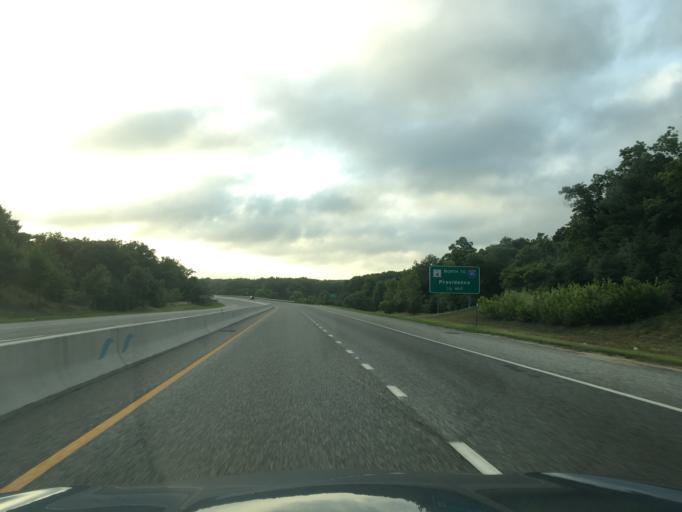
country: US
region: Rhode Island
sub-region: Kent County
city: East Greenwich
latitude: 41.6258
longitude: -71.4756
